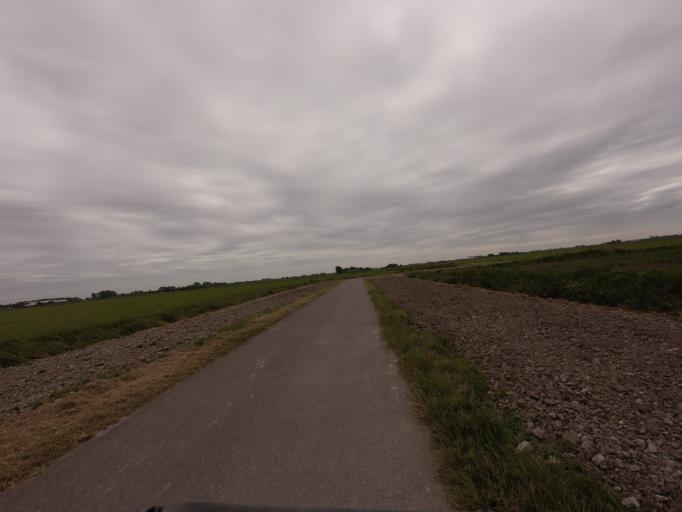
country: NL
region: North Holland
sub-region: Gemeente Medemblik
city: Opperdoes
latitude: 52.7334
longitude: 5.0569
